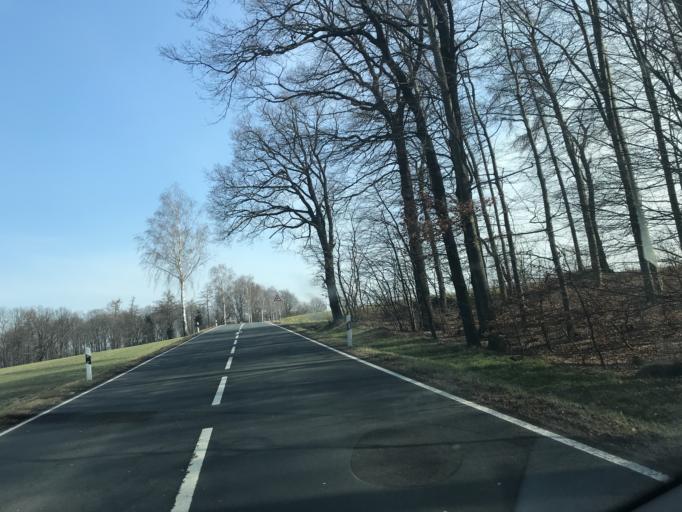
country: DE
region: Saxony
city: Rochlitz
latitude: 51.0376
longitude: 12.7748
